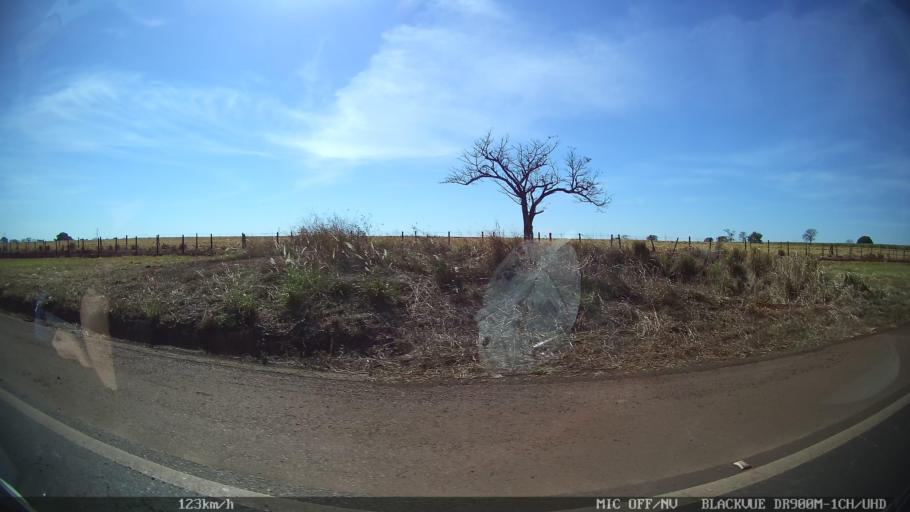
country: BR
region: Sao Paulo
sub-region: Ipua
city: Ipua
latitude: -20.4759
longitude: -48.0925
